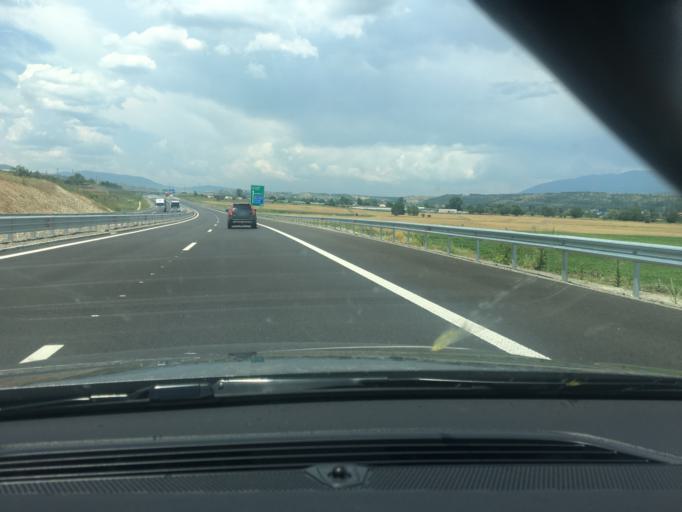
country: BG
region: Blagoevgrad
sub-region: Obshtina Blagoevgrad
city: Blagoevgrad
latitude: 41.9985
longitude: 23.0524
